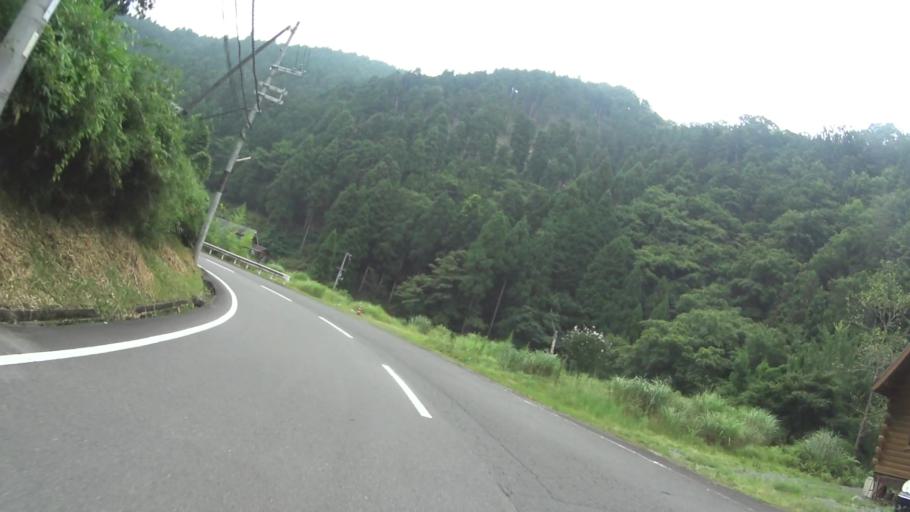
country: JP
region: Kyoto
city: Kameoka
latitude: 35.1495
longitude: 135.5936
